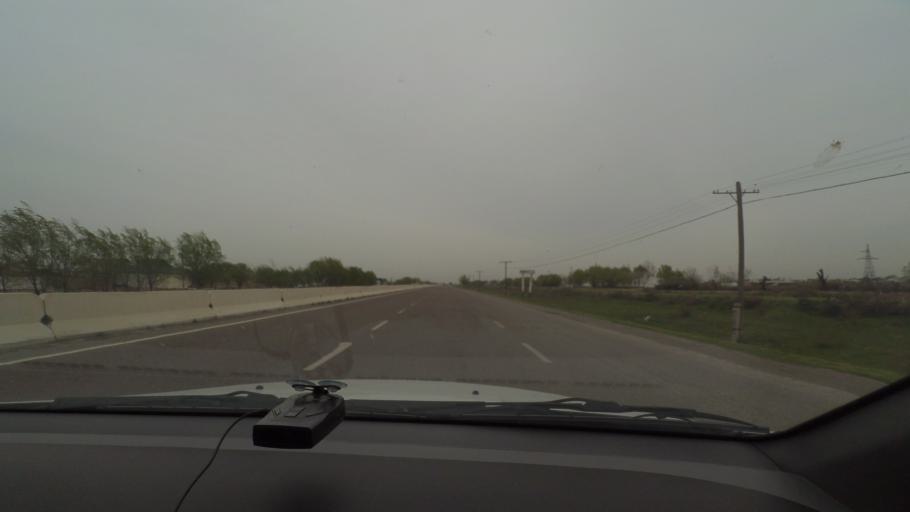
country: UZ
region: Sirdaryo
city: Guliston
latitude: 40.4926
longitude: 68.6825
